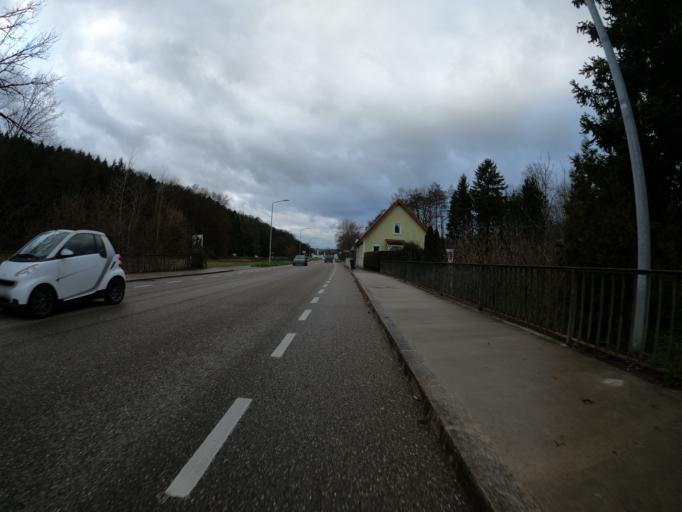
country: DE
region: Baden-Wuerttemberg
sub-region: Regierungsbezirk Stuttgart
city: Waldstetten
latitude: 48.7853
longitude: 9.8295
